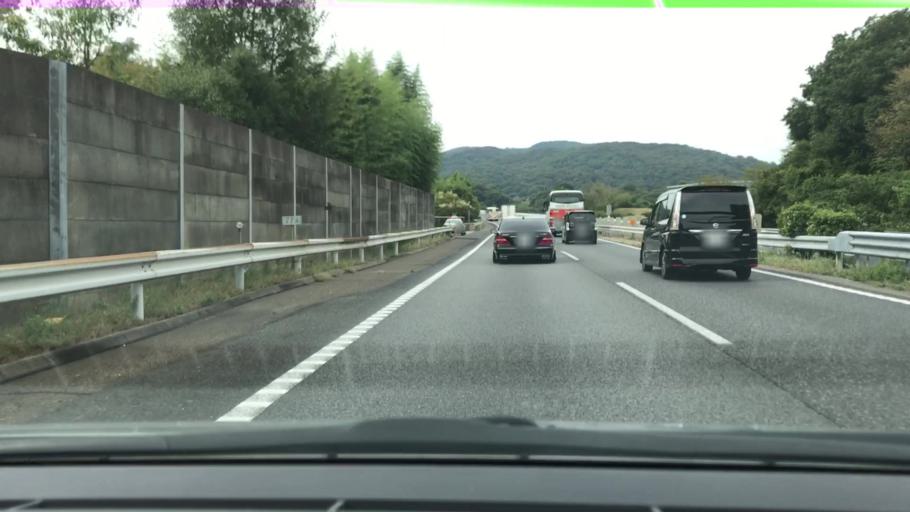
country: JP
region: Hyogo
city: Aioi
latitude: 34.8243
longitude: 134.4666
